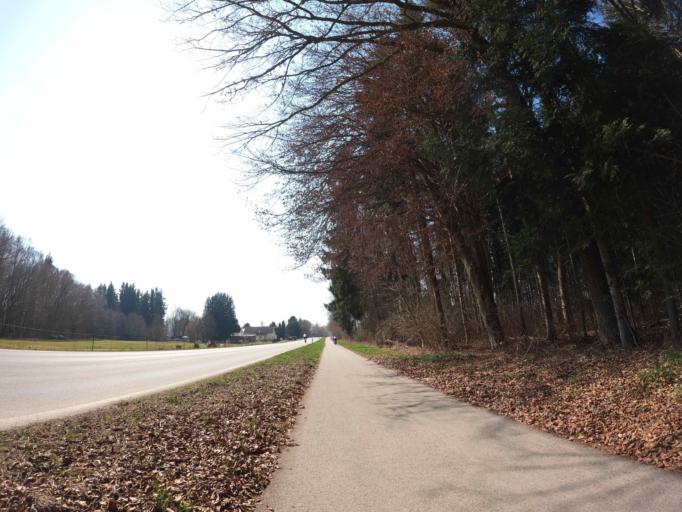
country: DE
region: Bavaria
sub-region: Upper Bavaria
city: Schaftlarn
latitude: 48.0227
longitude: 11.4182
